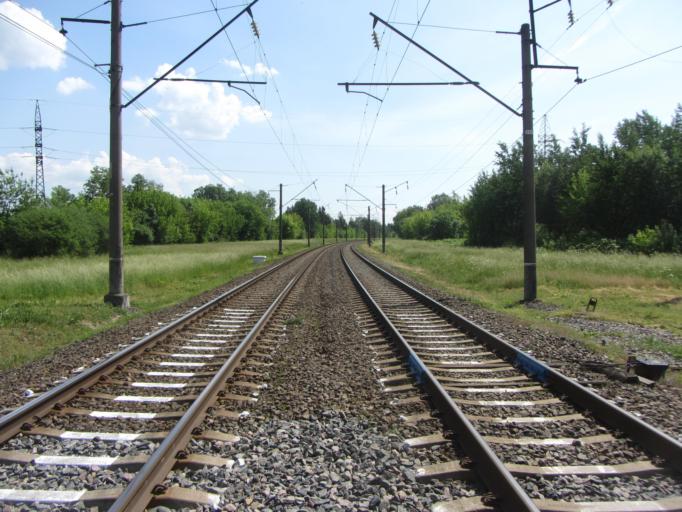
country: LT
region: Kauno apskritis
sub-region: Kauno rajonas
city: Karmelava
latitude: 54.9233
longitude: 24.0914
